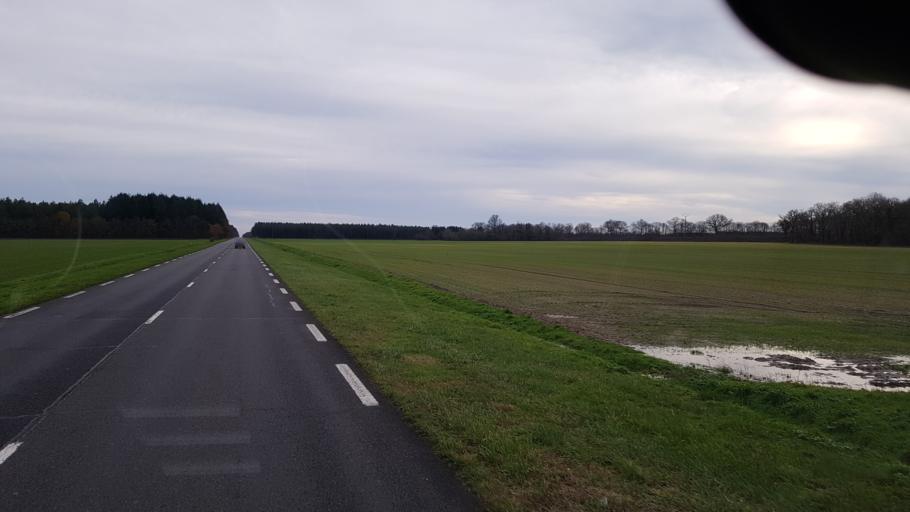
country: FR
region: Centre
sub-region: Departement du Loir-et-Cher
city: Lamotte-Beuvron
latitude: 47.6422
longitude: 1.9957
